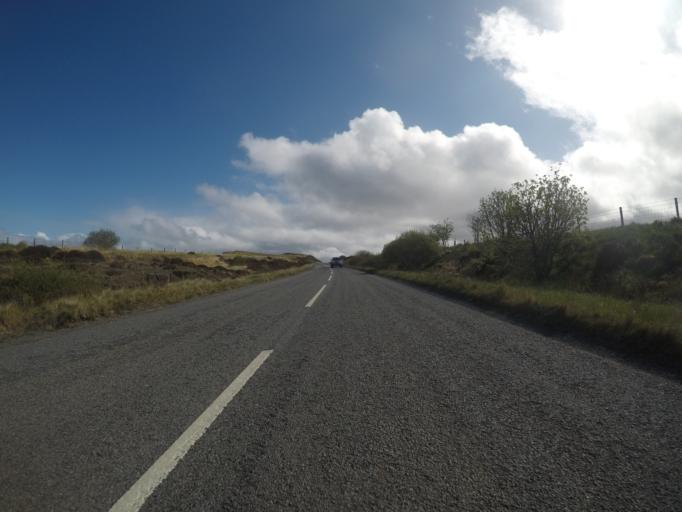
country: GB
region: Scotland
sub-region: Highland
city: Portree
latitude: 57.5738
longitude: -6.1545
